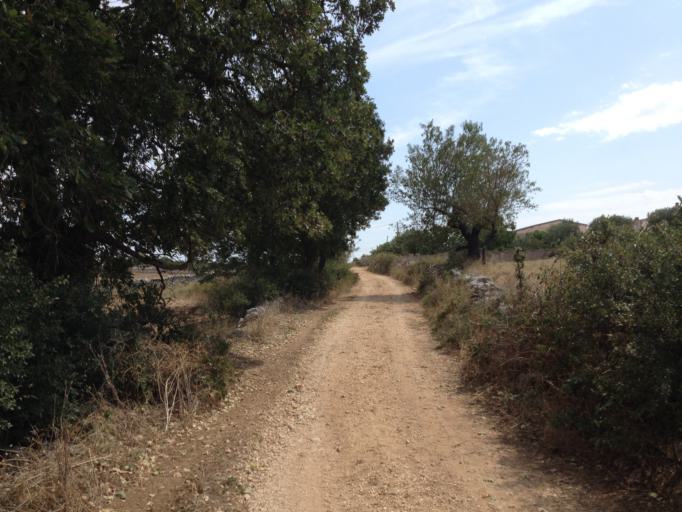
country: IT
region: Apulia
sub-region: Provincia di Bari
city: Gioia del Colle
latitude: 40.8240
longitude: 16.9766
